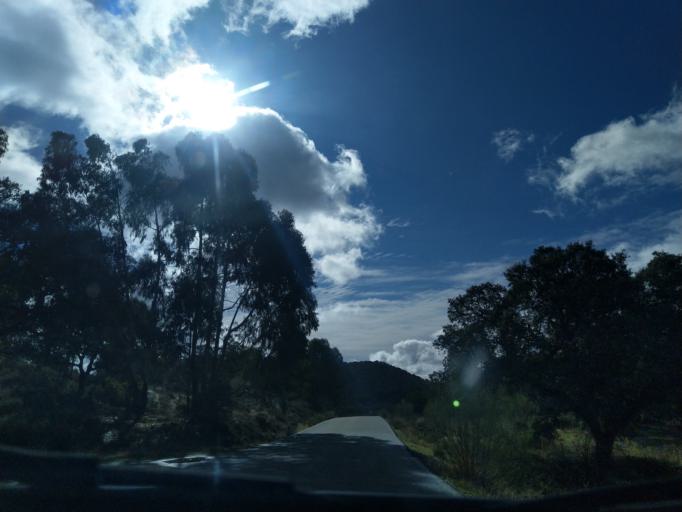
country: ES
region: Extremadura
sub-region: Provincia de Badajoz
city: Reina
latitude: 38.1281
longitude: -5.9148
